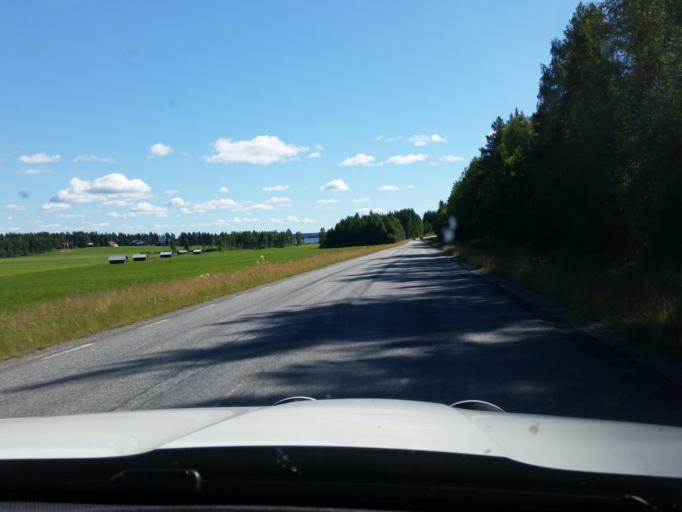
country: SE
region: Norrbotten
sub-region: Pitea Kommun
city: Roknas
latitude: 65.3191
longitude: 21.2674
